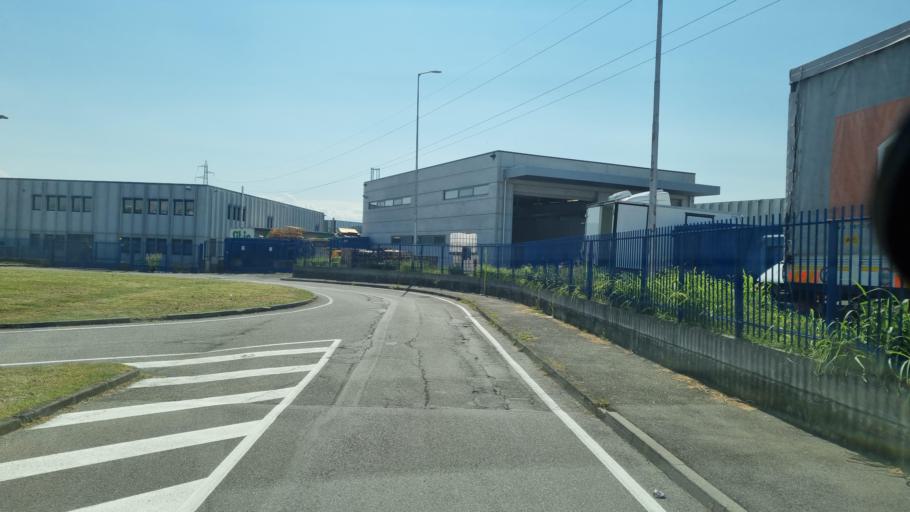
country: IT
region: Lombardy
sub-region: Provincia di Bergamo
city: Lallio
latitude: 45.6519
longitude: 9.6240
